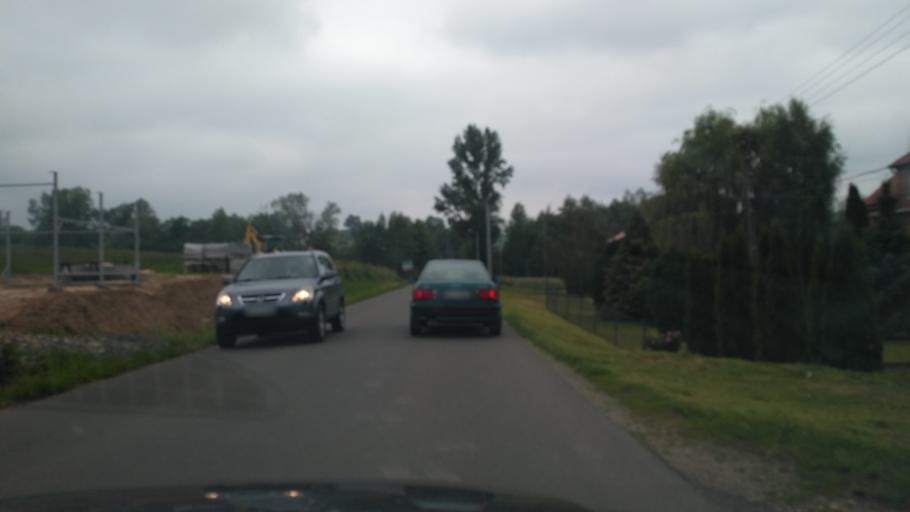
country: PL
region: Subcarpathian Voivodeship
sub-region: Powiat ropczycko-sedziszowski
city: Sedziszow Malopolski
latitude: 50.0448
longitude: 21.6998
